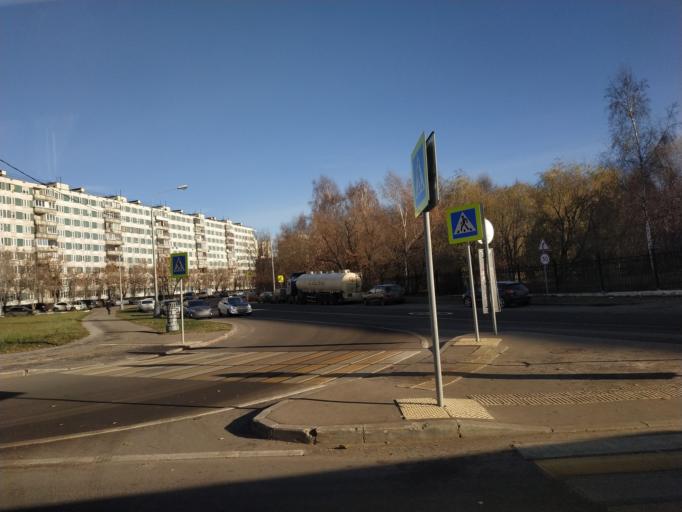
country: RU
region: Moscow
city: Zagor'ye
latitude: 55.5764
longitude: 37.6770
